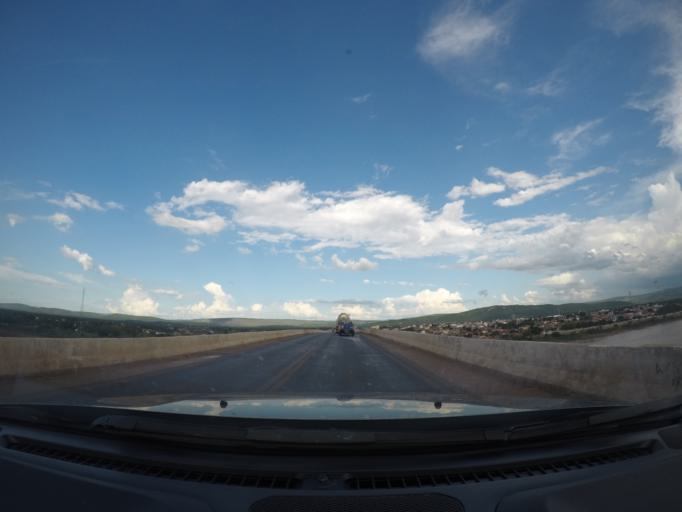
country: BR
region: Bahia
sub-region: Ibotirama
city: Ibotirama
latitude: -12.1806
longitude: -43.2271
